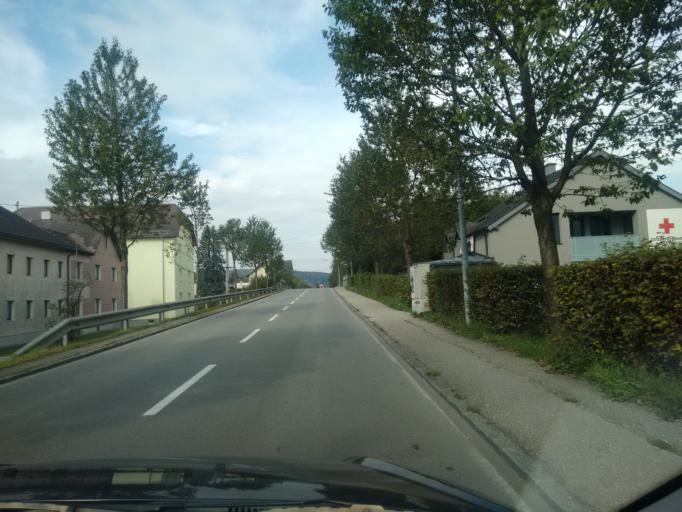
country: AT
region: Upper Austria
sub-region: Politischer Bezirk Vocklabruck
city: Attnang-Puchheim
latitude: 48.0048
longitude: 13.7165
